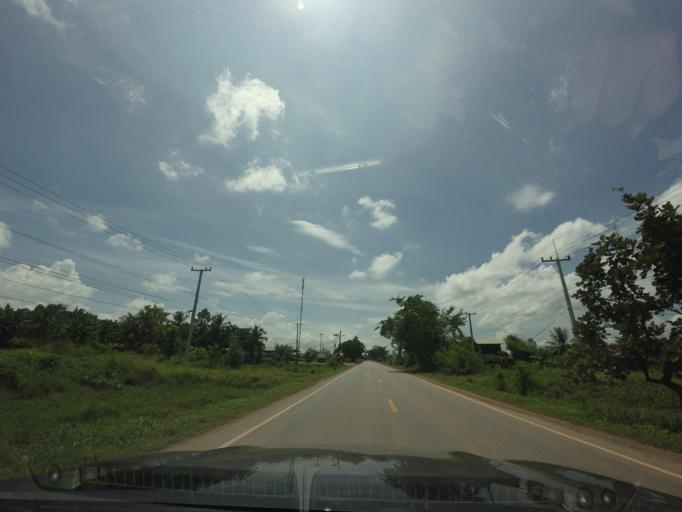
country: TH
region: Nong Khai
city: Pho Tak
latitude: 17.7691
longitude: 102.3965
